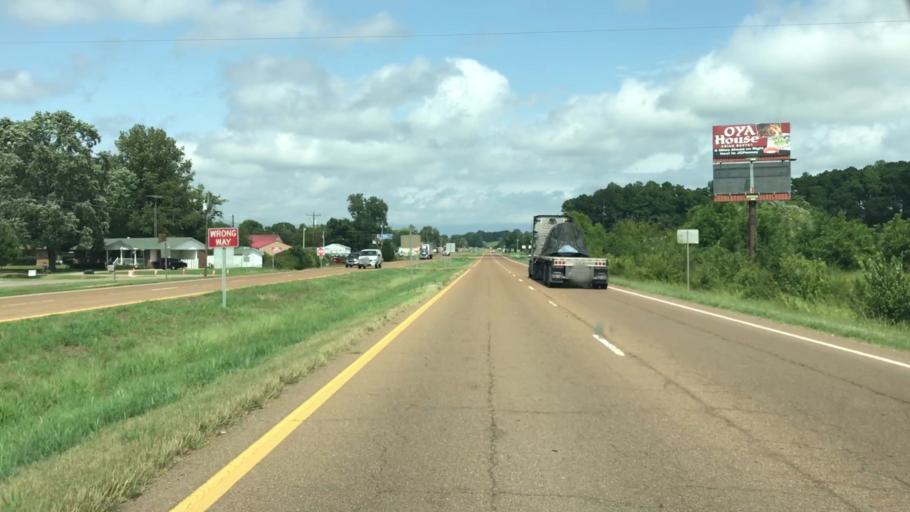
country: US
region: Tennessee
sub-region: Obion County
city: Troy
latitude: 36.3458
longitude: -89.1508
